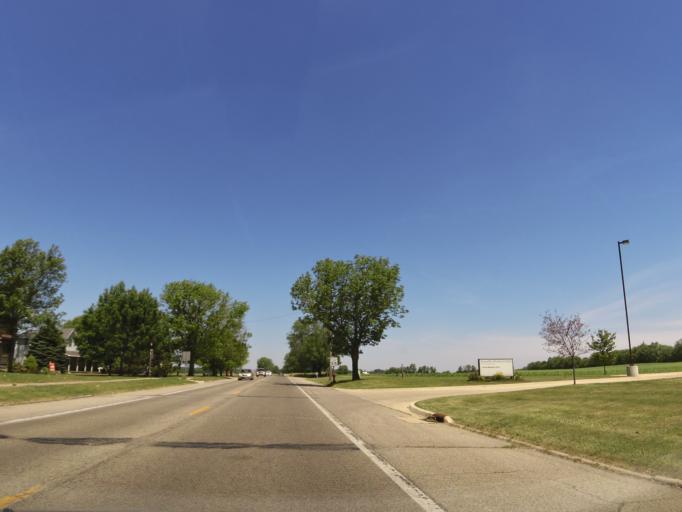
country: US
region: Illinois
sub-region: Vermilion County
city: Rossville
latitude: 40.3860
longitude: -87.6723
